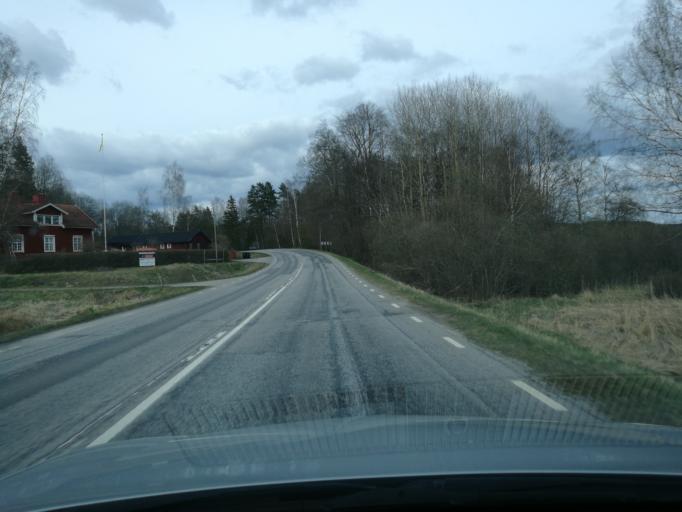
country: SE
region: Soedermanland
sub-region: Gnesta Kommun
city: Gnesta
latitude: 58.9034
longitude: 17.3209
